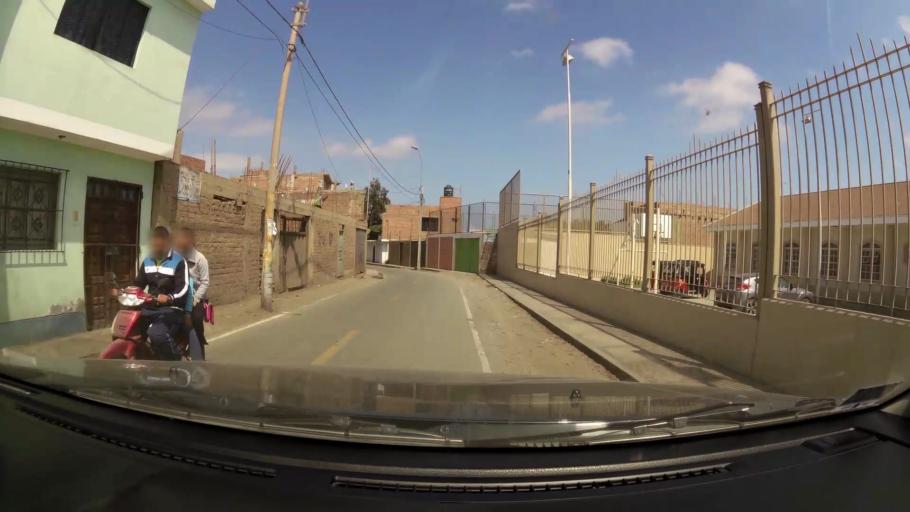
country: PE
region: Lima
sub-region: Provincia de Canete
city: Mala
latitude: -12.6558
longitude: -76.6315
